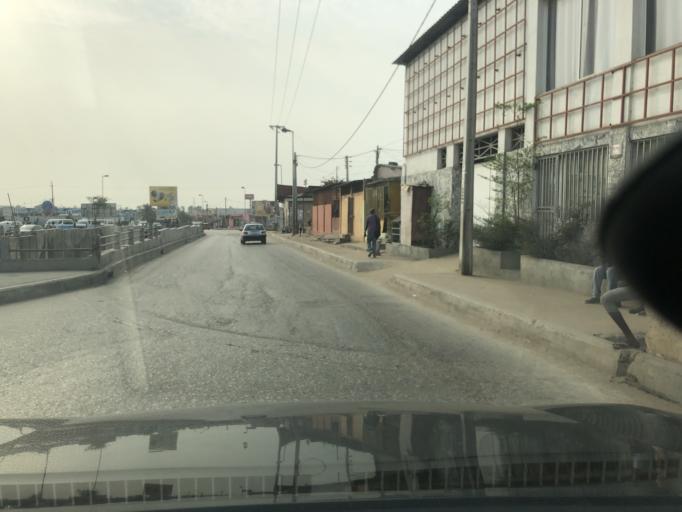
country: AO
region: Luanda
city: Luanda
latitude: -8.8485
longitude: 13.2138
